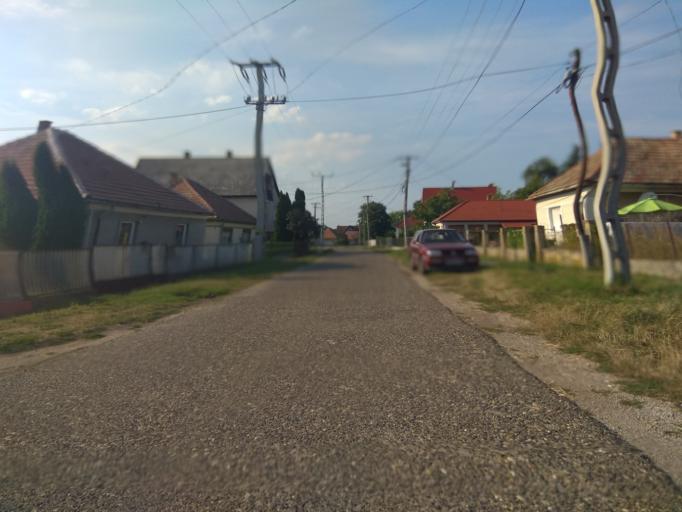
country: HU
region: Borsod-Abauj-Zemplen
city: Harsany
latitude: 47.9215
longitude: 20.7393
